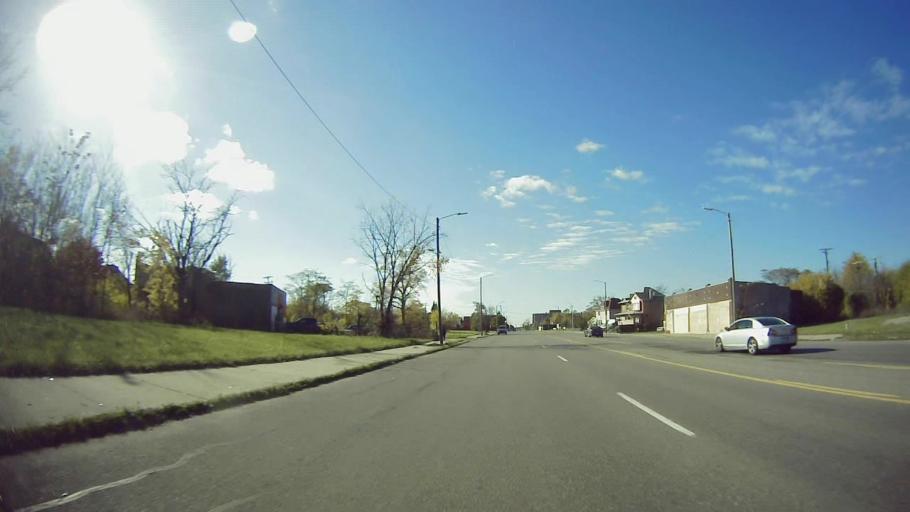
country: US
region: Michigan
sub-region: Wayne County
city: Detroit
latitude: 42.3448
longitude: -83.1021
